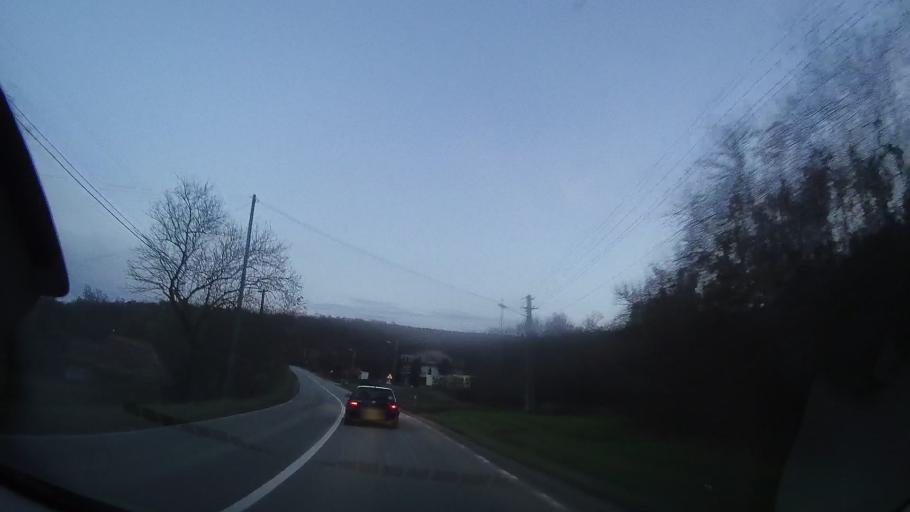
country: RO
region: Cluj
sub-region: Comuna Mociu
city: Mociu
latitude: 46.7928
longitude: 24.0562
